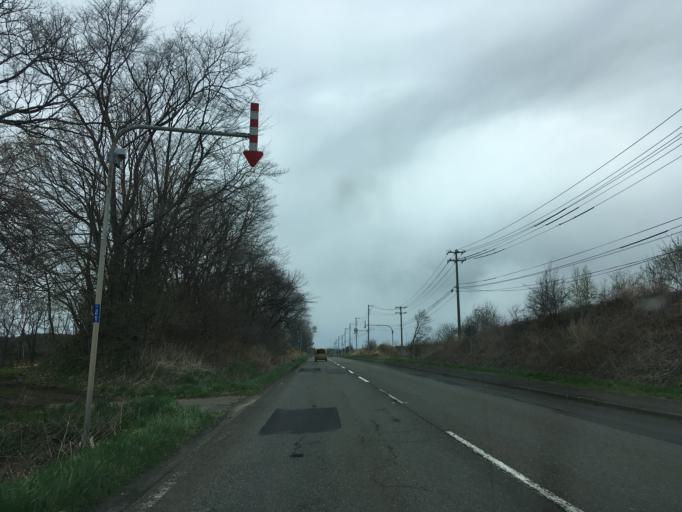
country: JP
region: Hokkaido
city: Chitose
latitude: 42.9001
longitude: 141.8137
